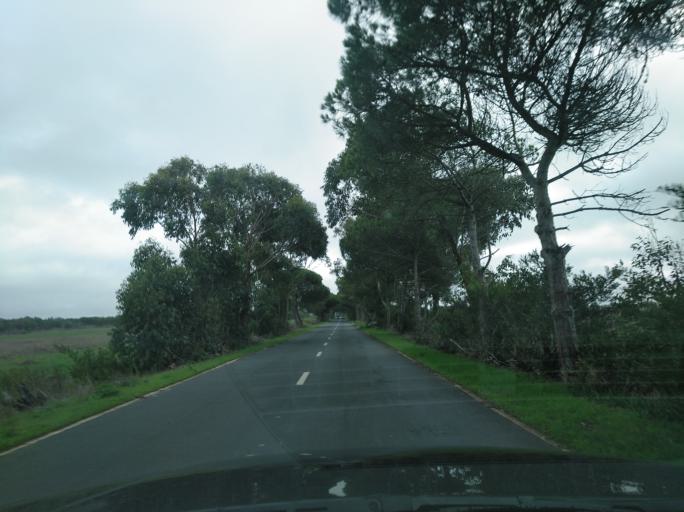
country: PT
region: Beja
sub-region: Odemira
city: Vila Nova de Milfontes
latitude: 37.7103
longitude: -8.7765
